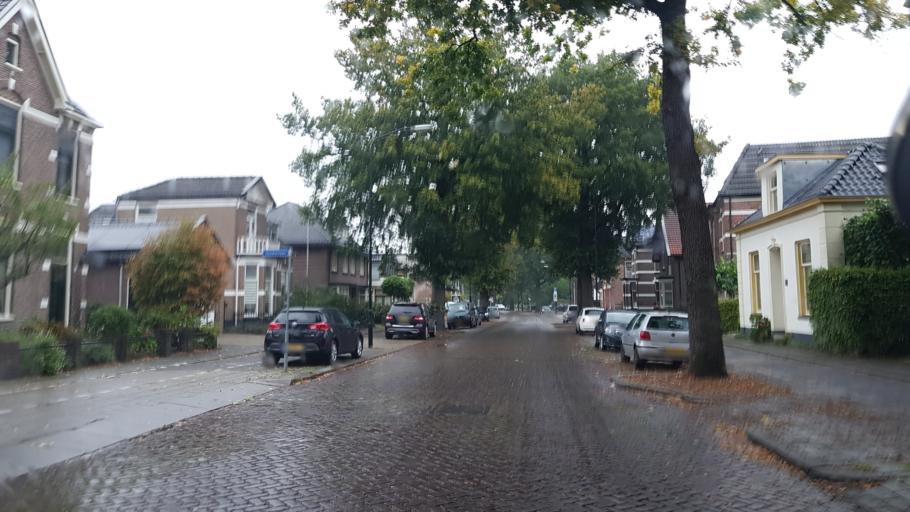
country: NL
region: Gelderland
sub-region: Gemeente Apeldoorn
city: Apeldoorn
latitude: 52.2064
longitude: 5.9630
